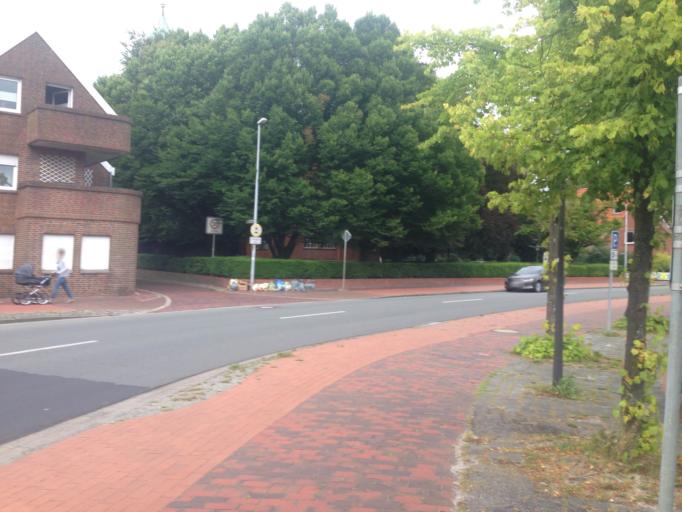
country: DE
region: Lower Saxony
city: Leer
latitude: 53.2268
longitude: 7.4464
